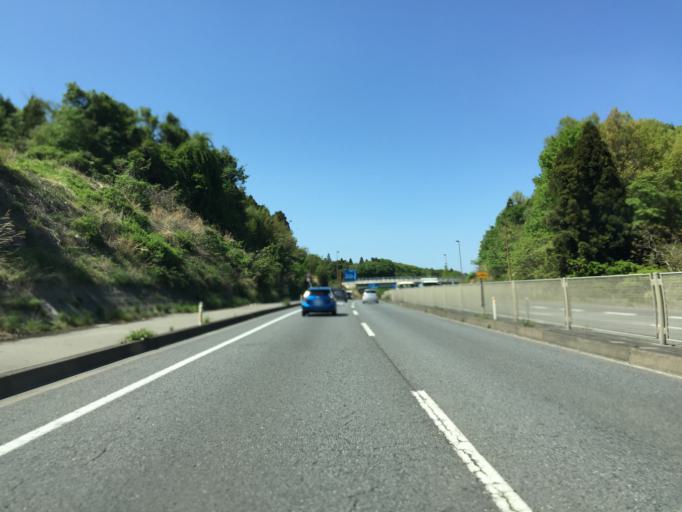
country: JP
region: Fukushima
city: Iwaki
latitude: 37.0170
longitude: 140.8942
